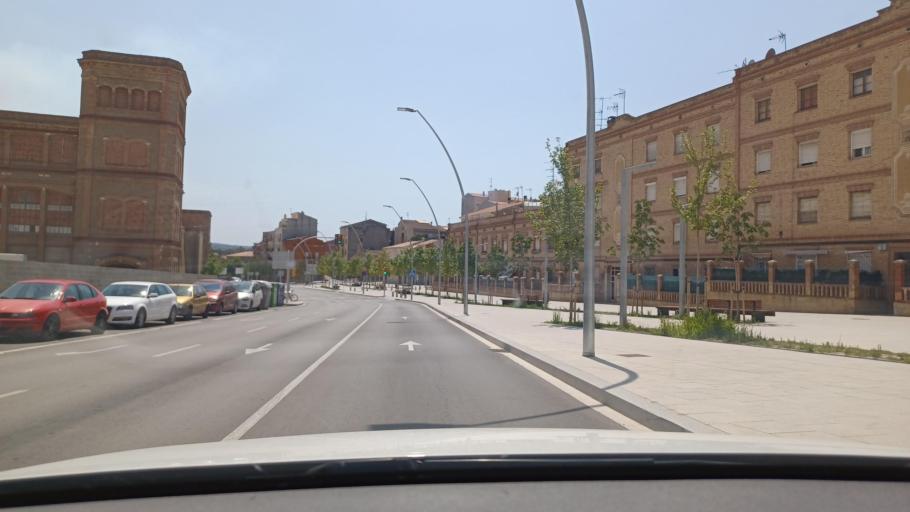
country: ES
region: Catalonia
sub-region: Provincia de Barcelona
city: Manresa
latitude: 41.7284
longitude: 1.8332
